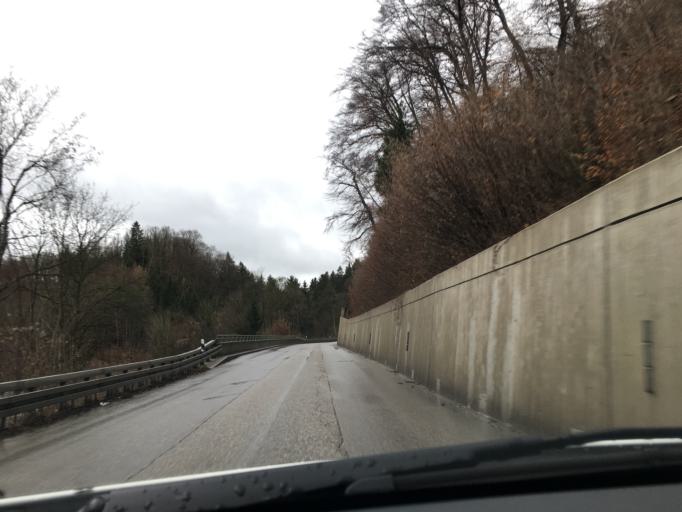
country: DE
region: Bavaria
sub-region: Upper Bavaria
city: Wolfratshausen
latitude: 47.9236
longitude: 11.4221
